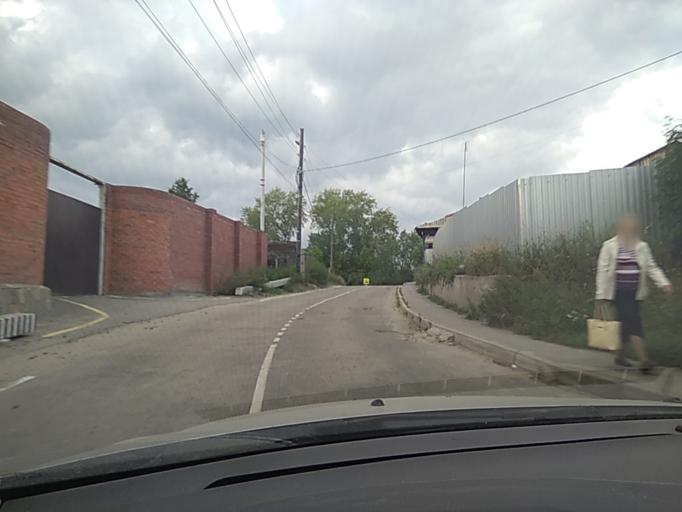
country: RU
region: Chelyabinsk
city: Kyshtym
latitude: 55.7007
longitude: 60.5311
